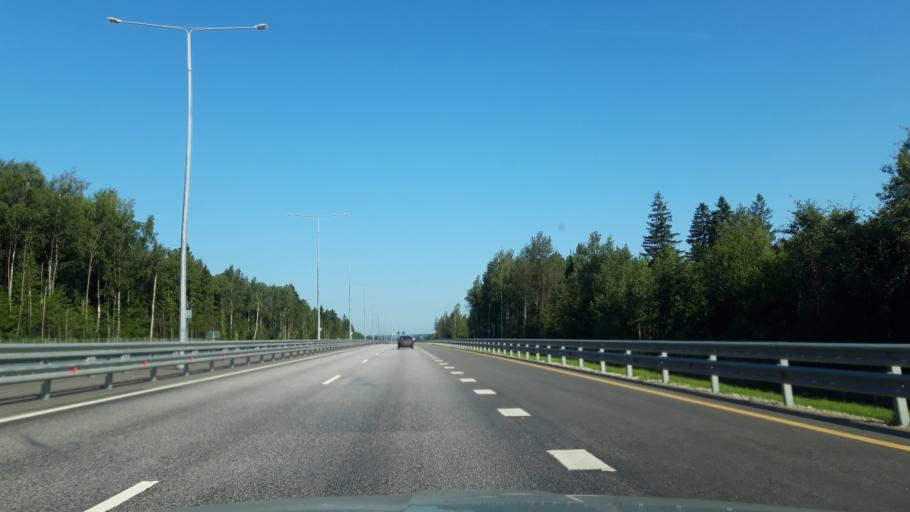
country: RU
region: Moskovskaya
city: Klin
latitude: 56.2823
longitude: 36.7140
